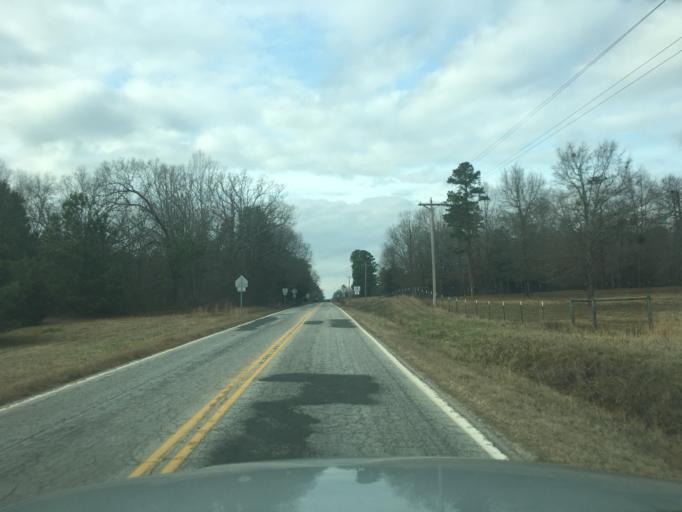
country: US
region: South Carolina
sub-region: Abbeville County
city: Due West
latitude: 34.2996
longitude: -82.4519
